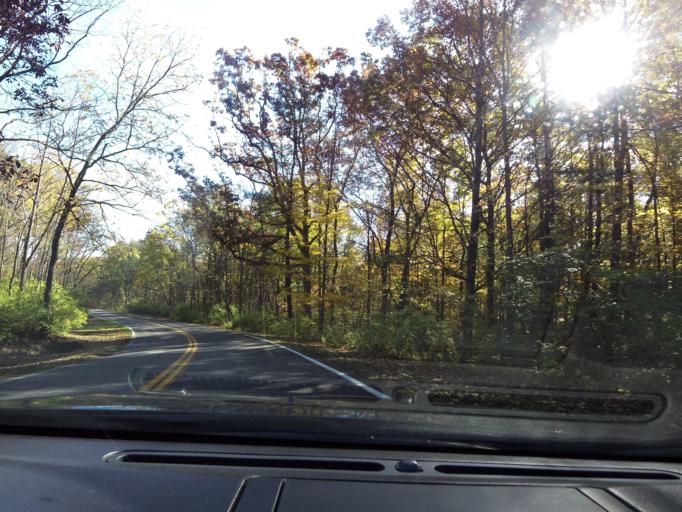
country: US
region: New York
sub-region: Wyoming County
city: Castile
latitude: 42.6378
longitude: -77.9892
